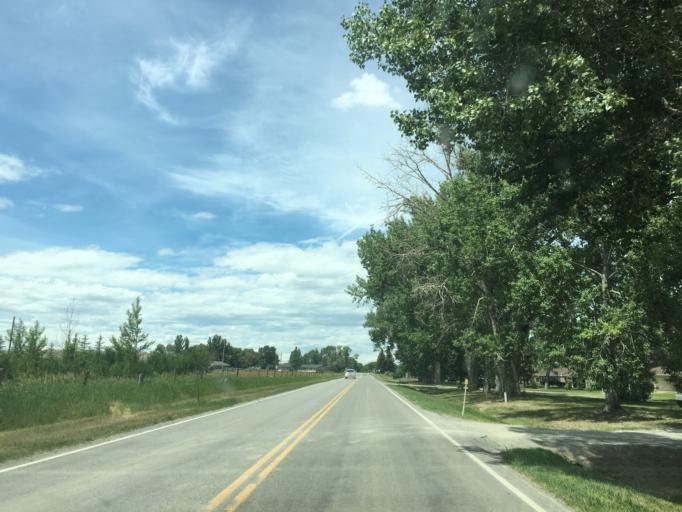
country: US
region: Montana
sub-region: Teton County
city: Choteau
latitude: 47.8247
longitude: -112.1933
